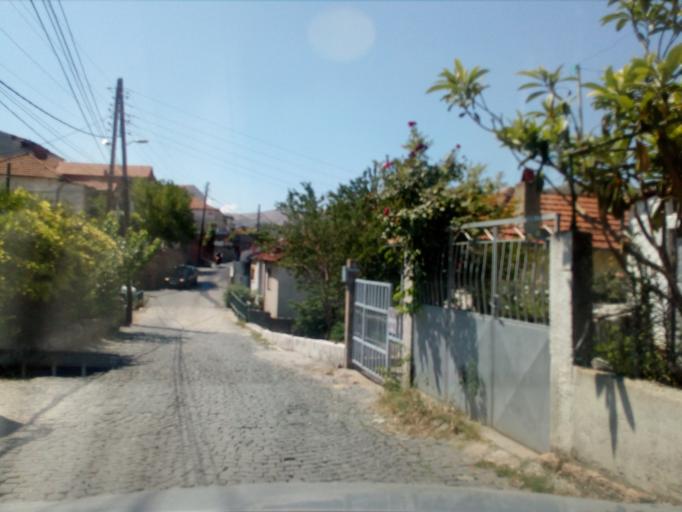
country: MK
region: Veles
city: Veles
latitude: 41.7178
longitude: 21.7887
